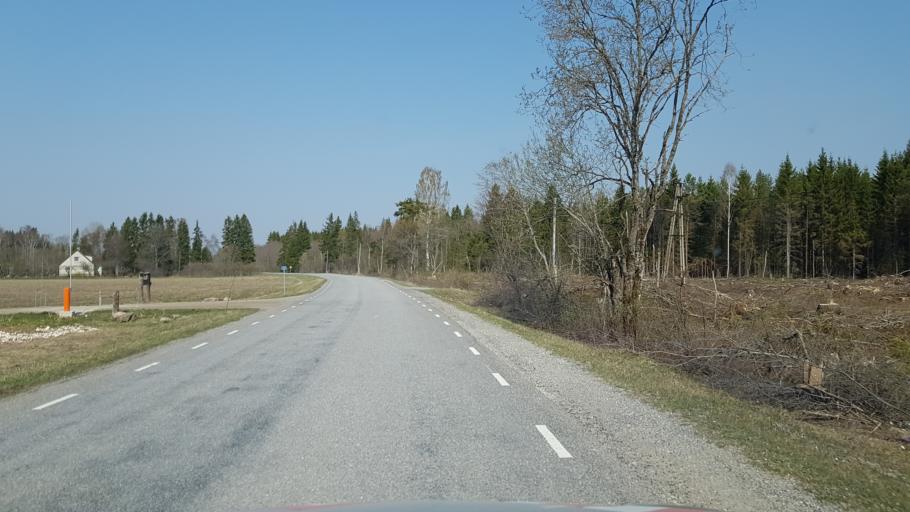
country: EE
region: Raplamaa
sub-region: Kohila vald
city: Kohila
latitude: 59.2006
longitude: 24.6691
